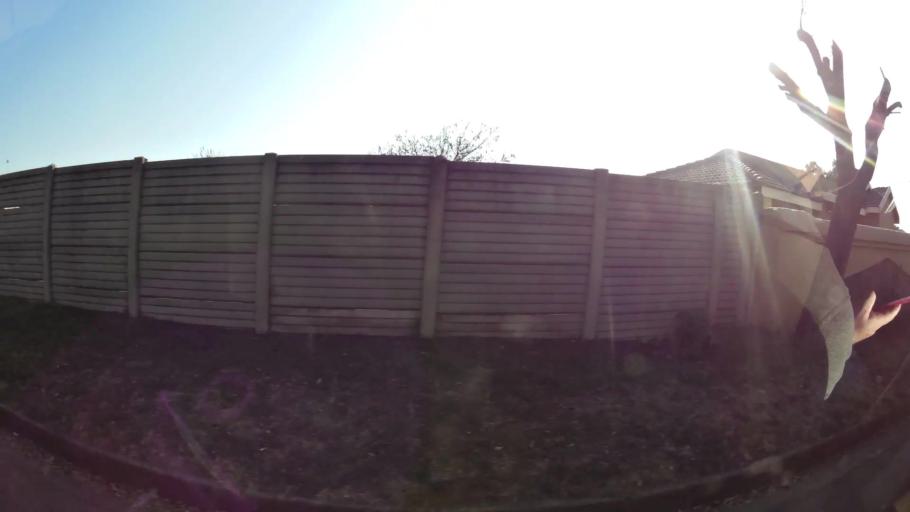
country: ZA
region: Gauteng
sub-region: City of Johannesburg Metropolitan Municipality
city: Modderfontein
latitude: -26.1572
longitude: 28.2027
